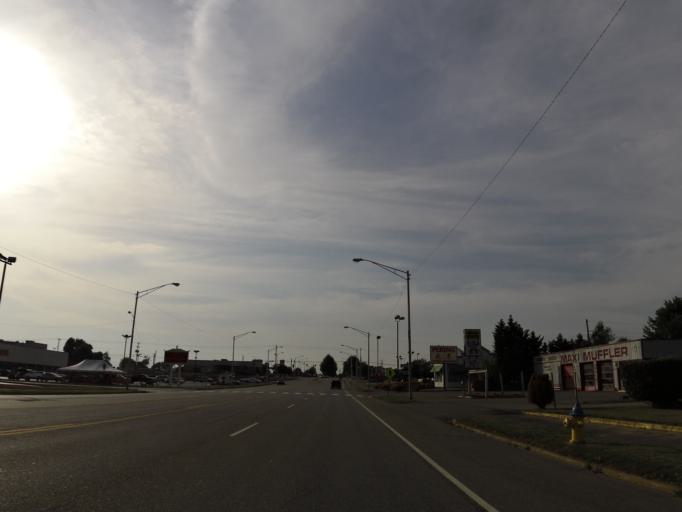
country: US
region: Tennessee
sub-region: Blount County
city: Maryville
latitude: 35.7650
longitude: -83.9710
